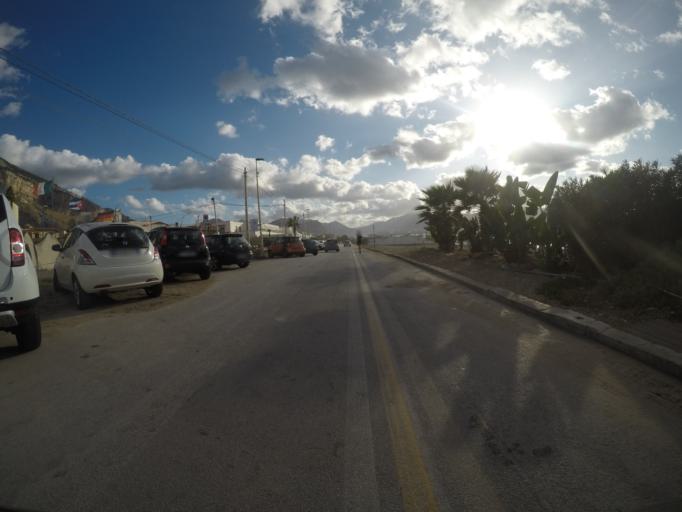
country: IT
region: Sicily
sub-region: Palermo
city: Isola delle Femmine
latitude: 38.1886
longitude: 13.2412
